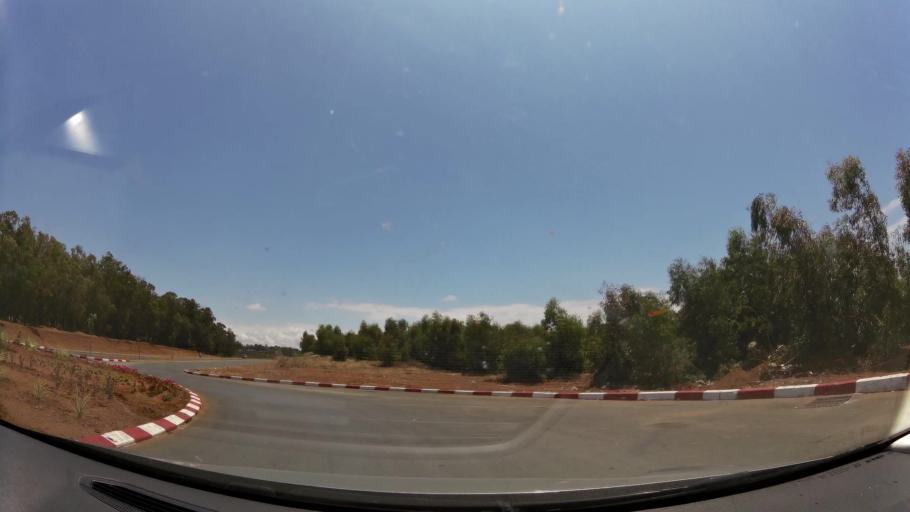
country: MA
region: Gharb-Chrarda-Beni Hssen
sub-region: Kenitra Province
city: Kenitra
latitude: 34.2466
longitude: -6.6390
